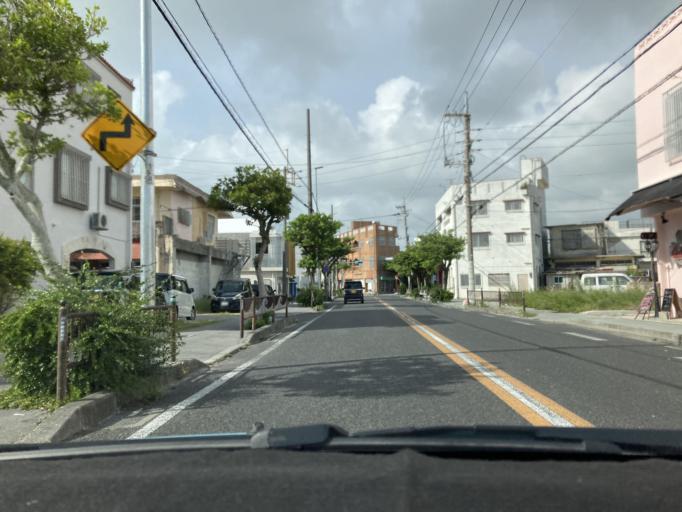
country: JP
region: Okinawa
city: Itoman
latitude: 26.1273
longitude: 127.6690
